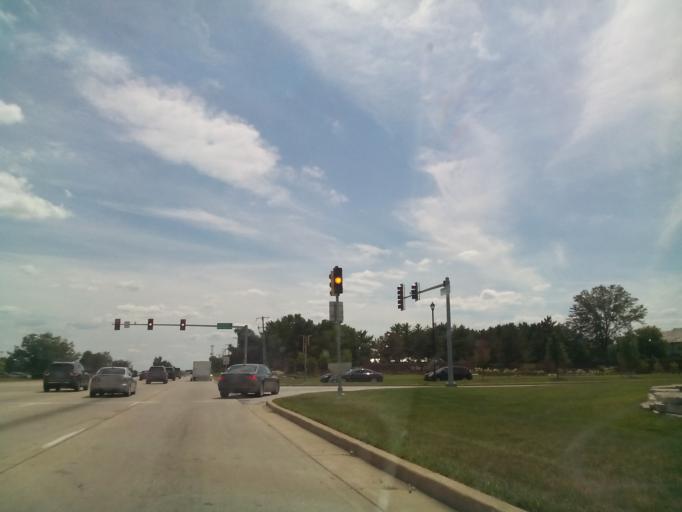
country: US
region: Illinois
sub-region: DuPage County
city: Naperville
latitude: 41.7273
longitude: -88.2063
